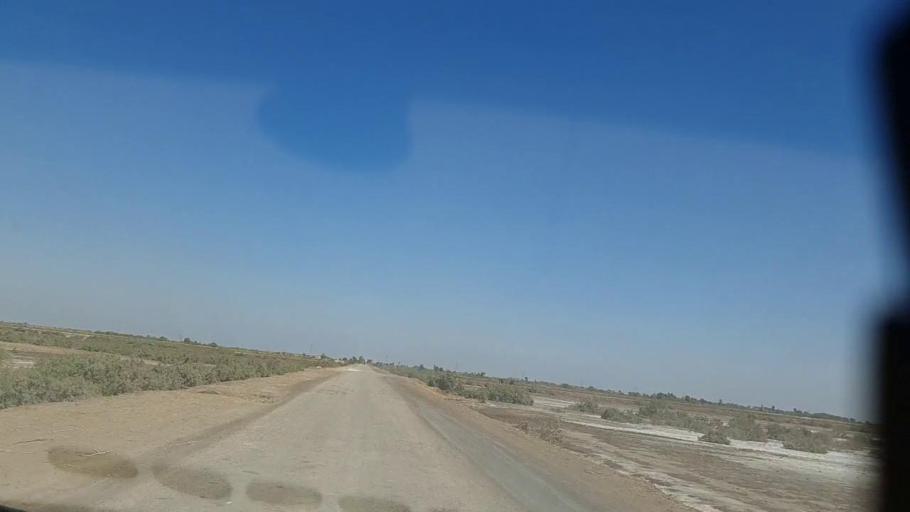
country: PK
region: Sindh
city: Mirwah Gorchani
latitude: 25.2424
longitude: 69.0306
